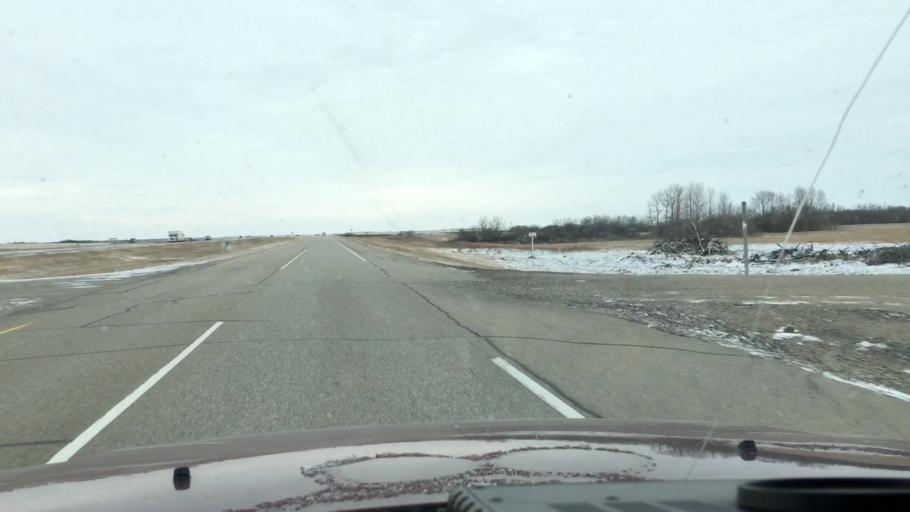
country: CA
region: Saskatchewan
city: Watrous
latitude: 51.3584
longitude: -106.1247
